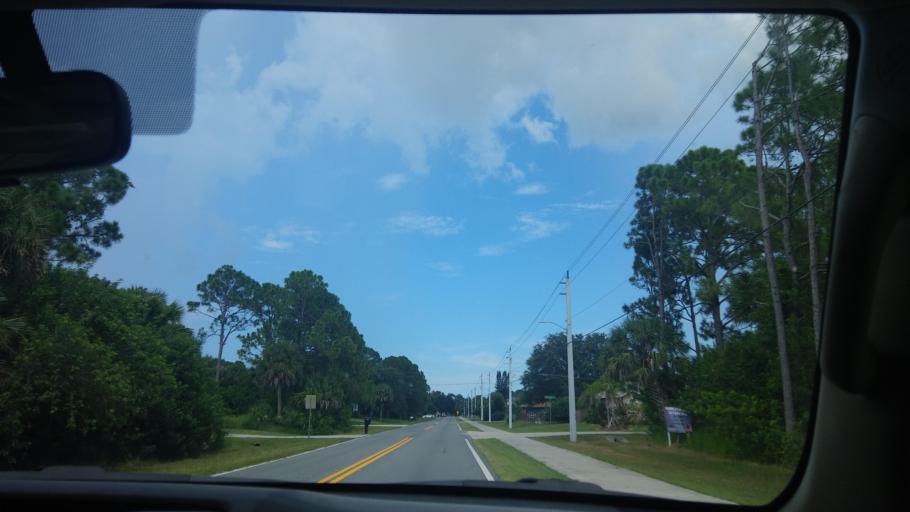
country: US
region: Florida
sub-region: Brevard County
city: West Melbourne
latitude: 28.0109
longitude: -80.6676
